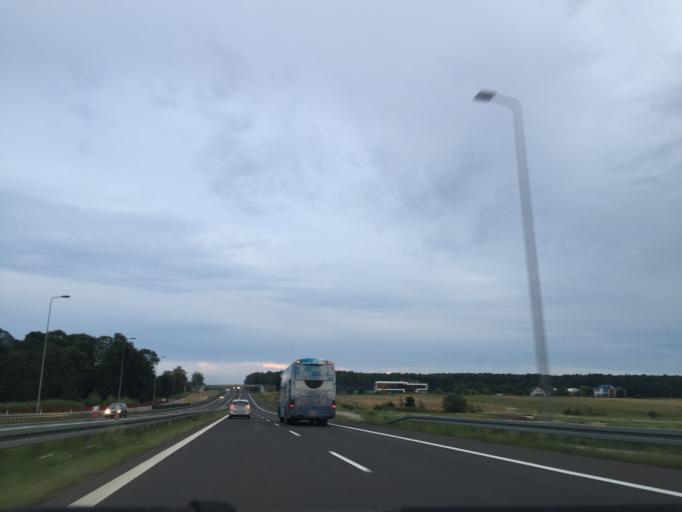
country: PL
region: Podlasie
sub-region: Powiat bialostocki
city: Choroszcz
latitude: 53.1588
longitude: 23.0008
